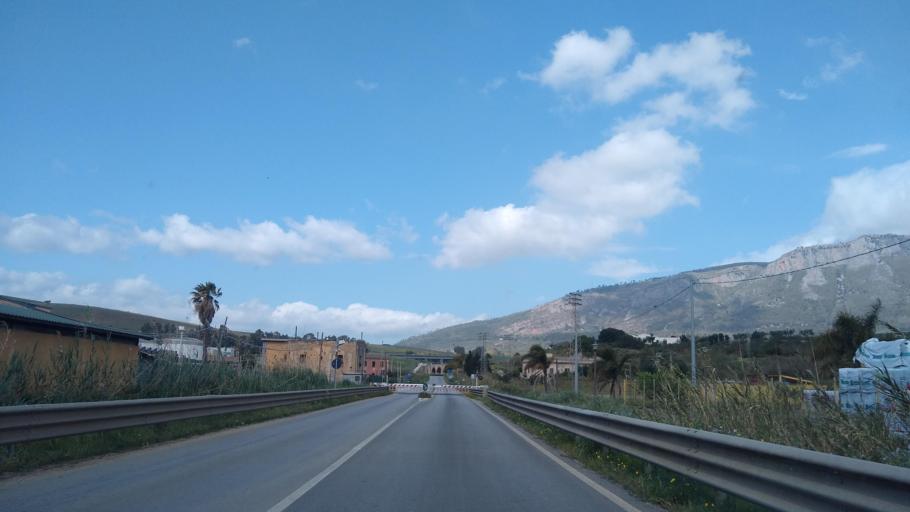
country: IT
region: Sicily
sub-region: Trapani
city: Alcamo
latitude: 37.9678
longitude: 12.9153
